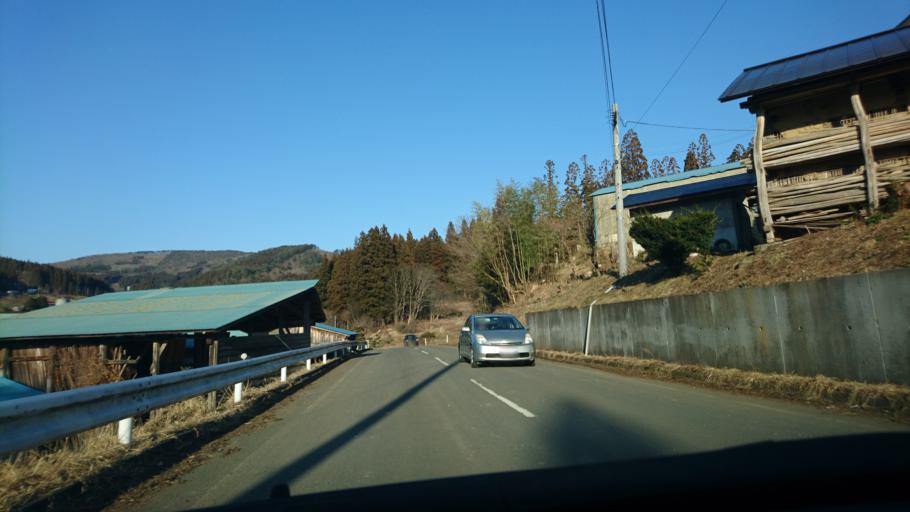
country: JP
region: Iwate
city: Ichinoseki
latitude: 38.8432
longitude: 141.3851
